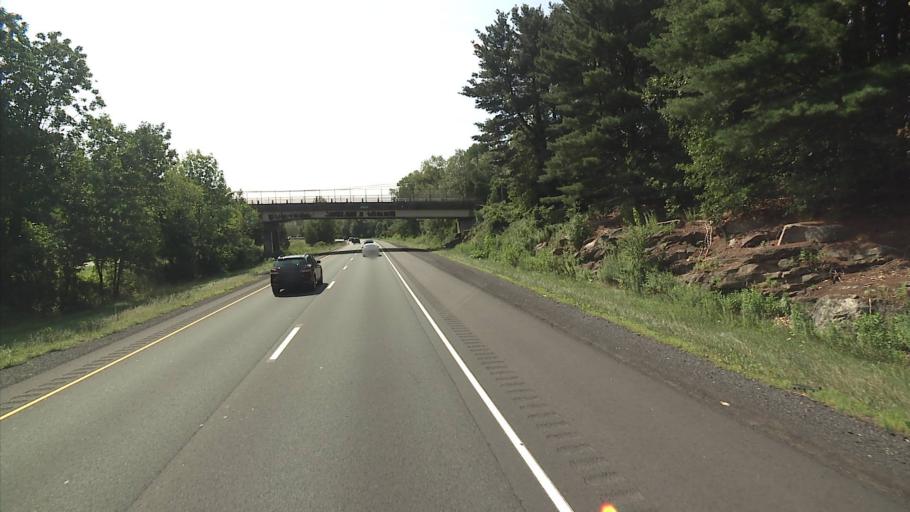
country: US
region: Connecticut
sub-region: Hartford County
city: Terramuggus
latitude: 41.6674
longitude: -72.5332
